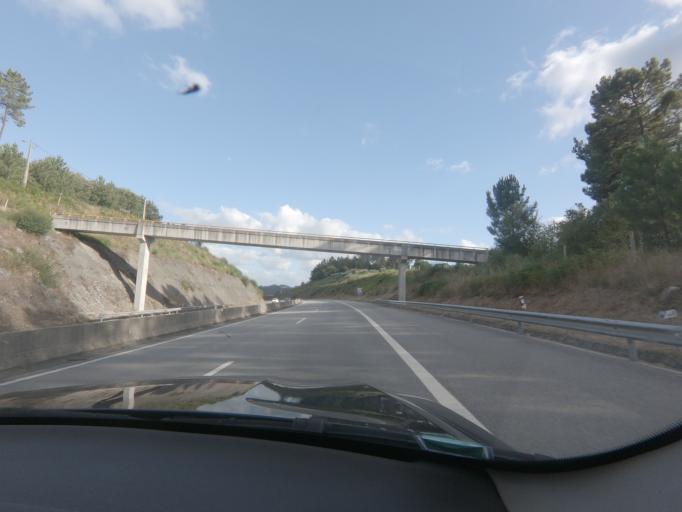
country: PT
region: Viseu
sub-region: Viseu
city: Abraveses
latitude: 40.6476
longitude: -7.9668
